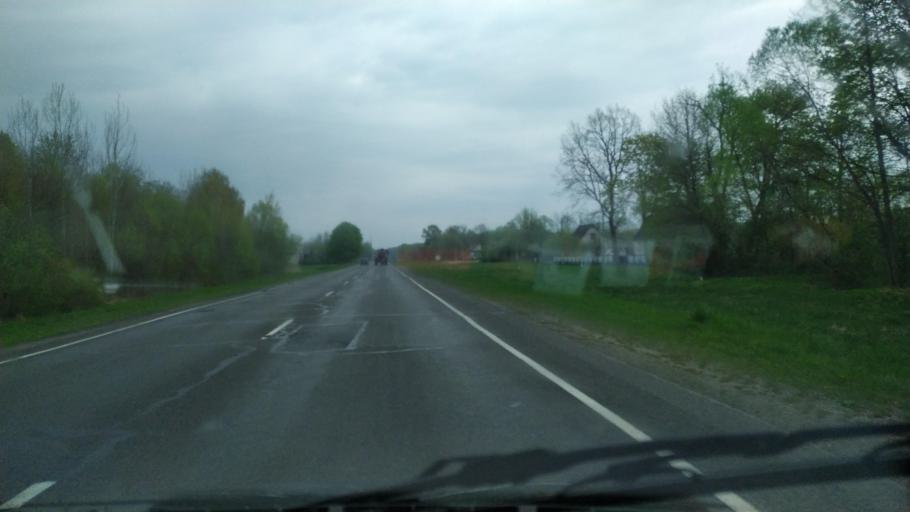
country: BY
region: Brest
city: Horad Kobryn
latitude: 52.3262
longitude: 24.5705
